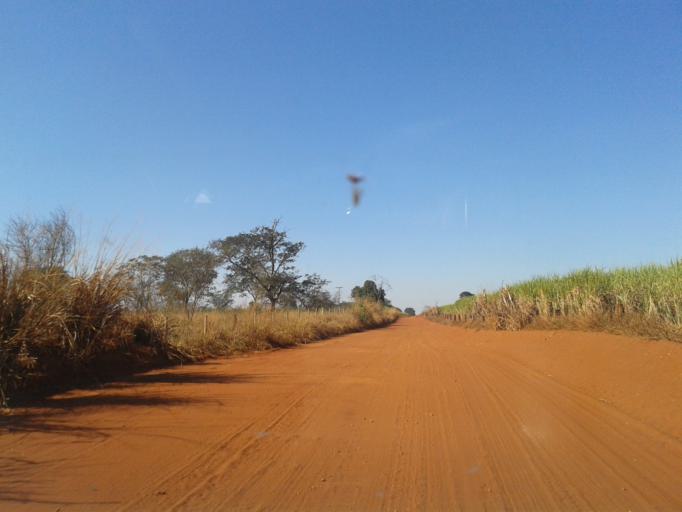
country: BR
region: Minas Gerais
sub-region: Santa Vitoria
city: Santa Vitoria
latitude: -18.8395
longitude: -50.0969
